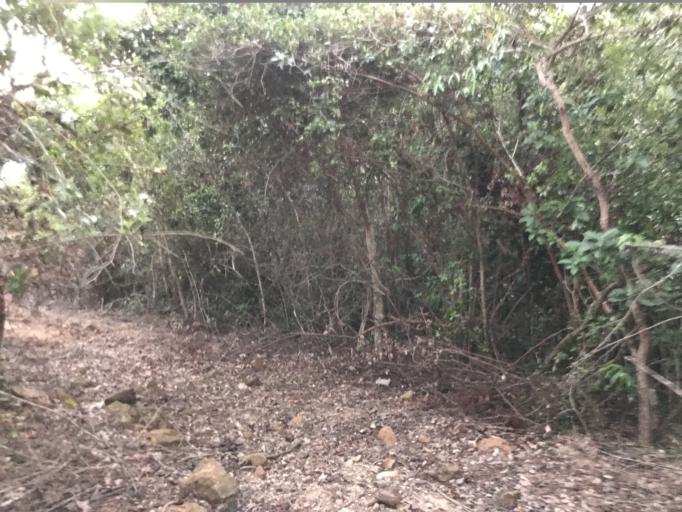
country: HK
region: Tai Po
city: Tai Po
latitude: 22.4721
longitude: 114.1455
